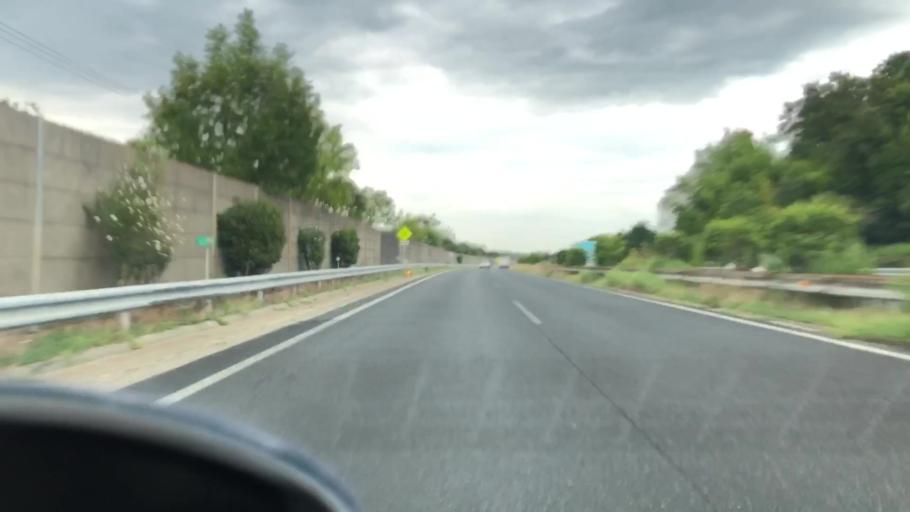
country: JP
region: Hyogo
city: Yashiro
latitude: 34.9180
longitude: 135.0152
